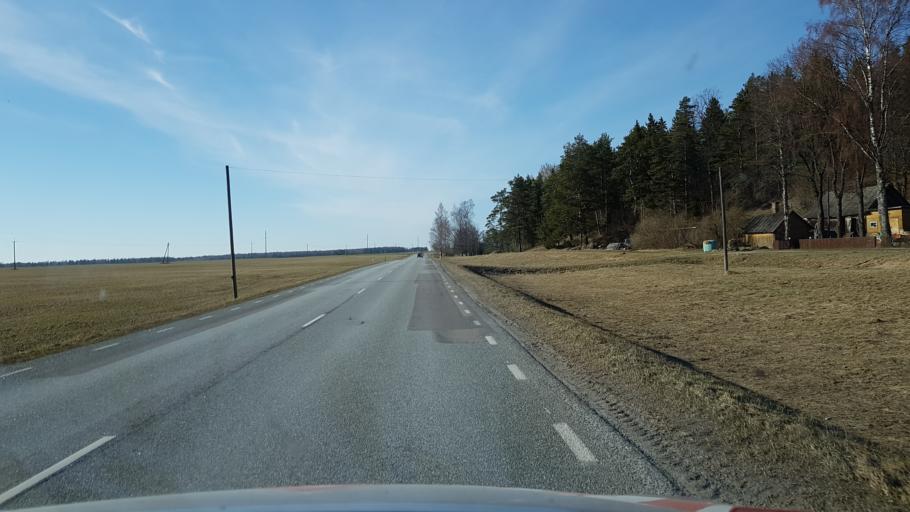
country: EE
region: Laeaene-Virumaa
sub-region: Vinni vald
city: Vinni
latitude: 59.1931
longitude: 26.5685
